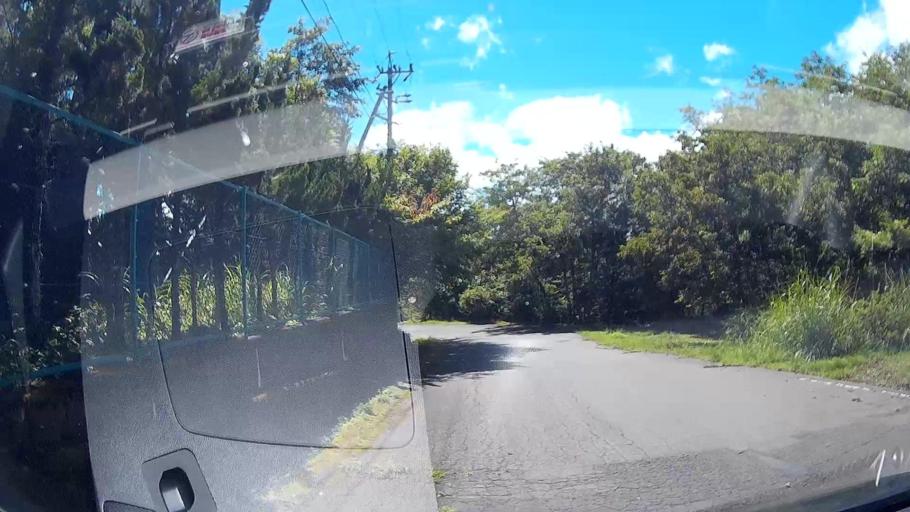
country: JP
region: Shizuoka
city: Shizuoka-shi
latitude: 35.2036
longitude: 138.2642
